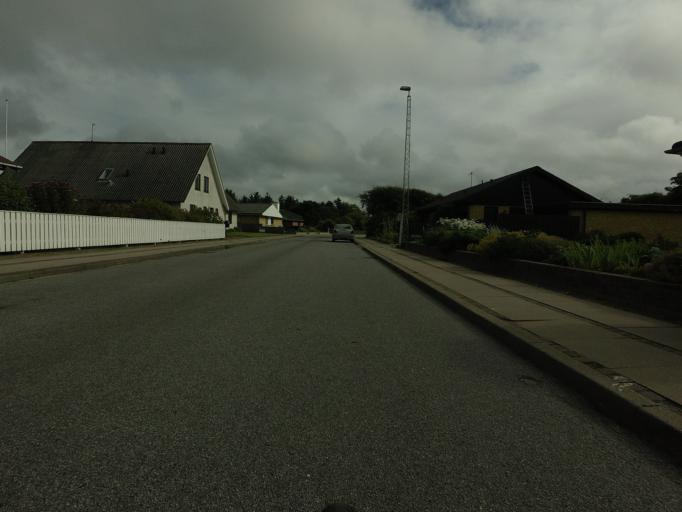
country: DK
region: North Denmark
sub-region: Jammerbugt Kommune
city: Pandrup
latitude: 57.3693
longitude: 9.7242
